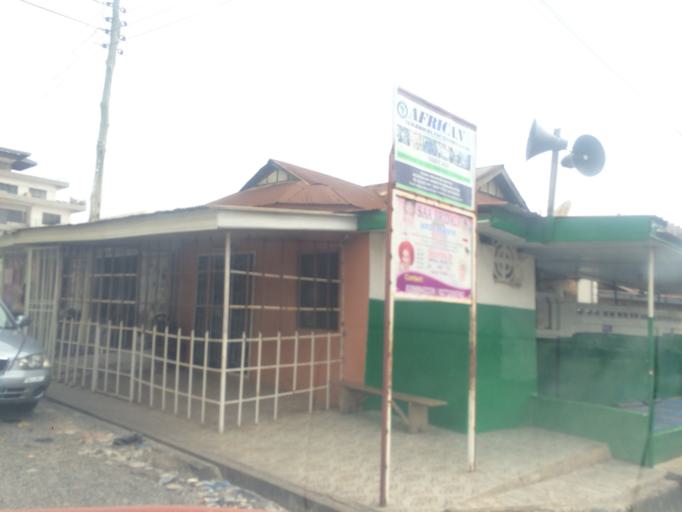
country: GH
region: Greater Accra
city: Accra
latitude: 5.5649
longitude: -0.2124
